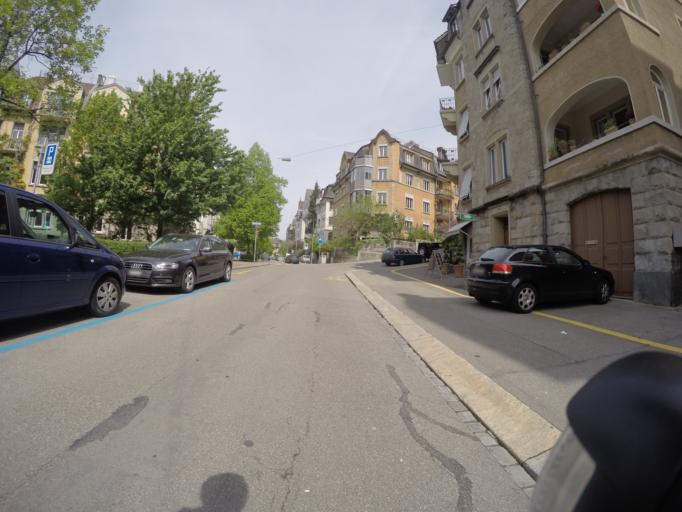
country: CH
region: Zurich
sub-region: Bezirk Zuerich
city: Zuerich (Kreis 6) / Oberstrass
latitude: 47.3833
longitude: 8.5454
